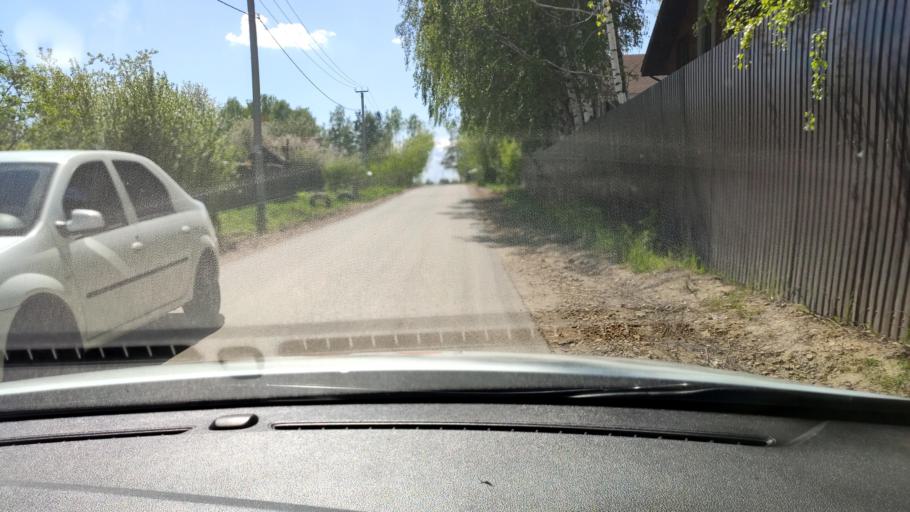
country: RU
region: Tatarstan
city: Vysokaya Gora
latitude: 55.8145
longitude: 49.2792
